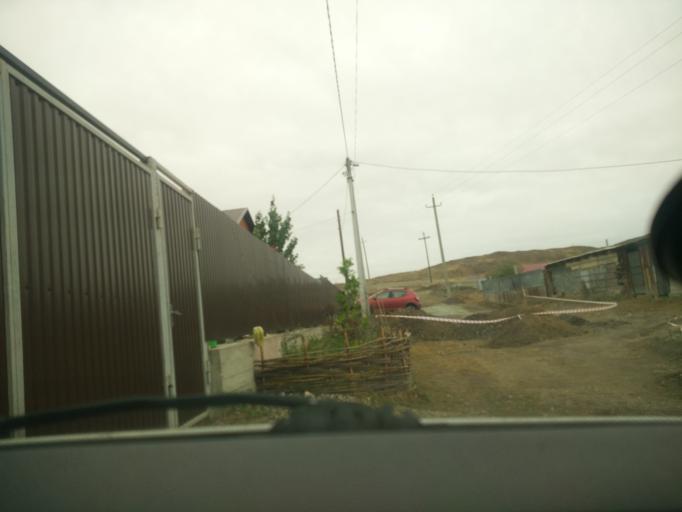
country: RU
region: Orenburg
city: Staraya Akkermanovka
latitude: 51.1516
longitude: 58.2282
